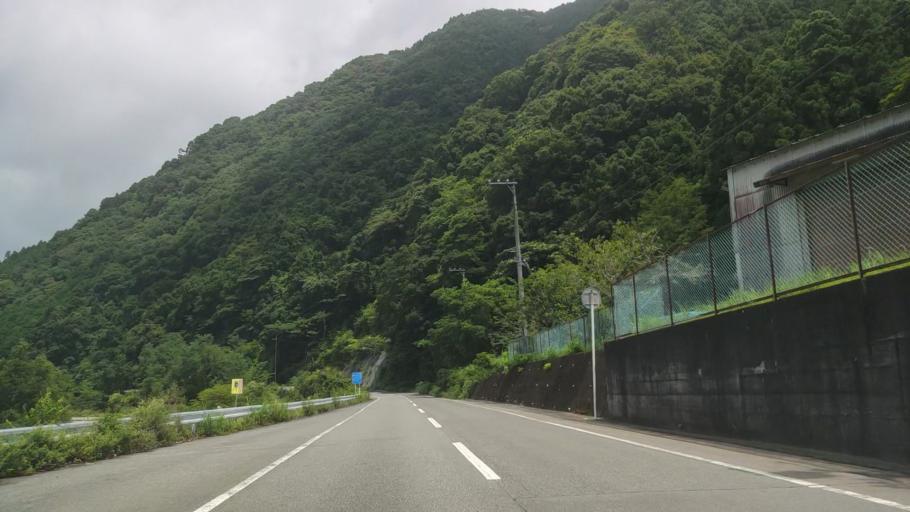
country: JP
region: Shizuoka
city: Fujinomiya
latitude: 35.2394
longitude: 138.5107
